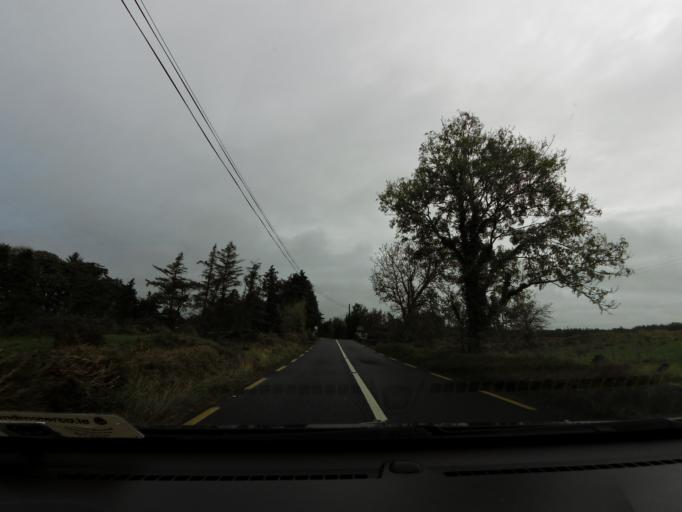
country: IE
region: Connaught
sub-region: Maigh Eo
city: Ballyhaunis
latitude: 53.6244
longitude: -8.7429
